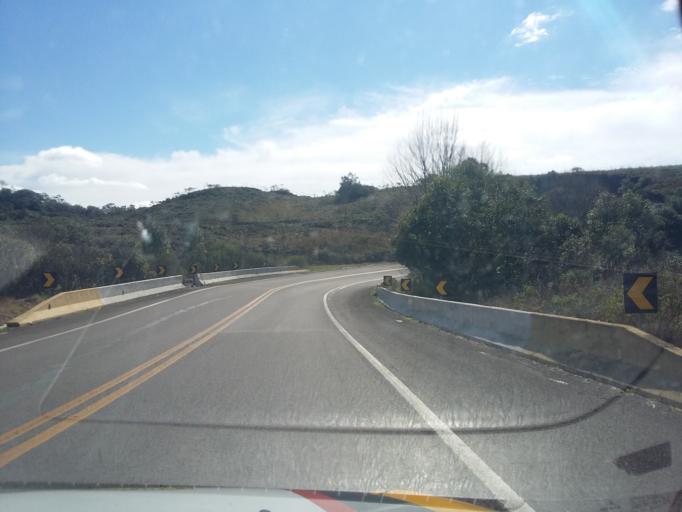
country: BR
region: Rio Grande do Sul
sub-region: Vacaria
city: Vacaria
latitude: -28.6609
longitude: -51.0586
